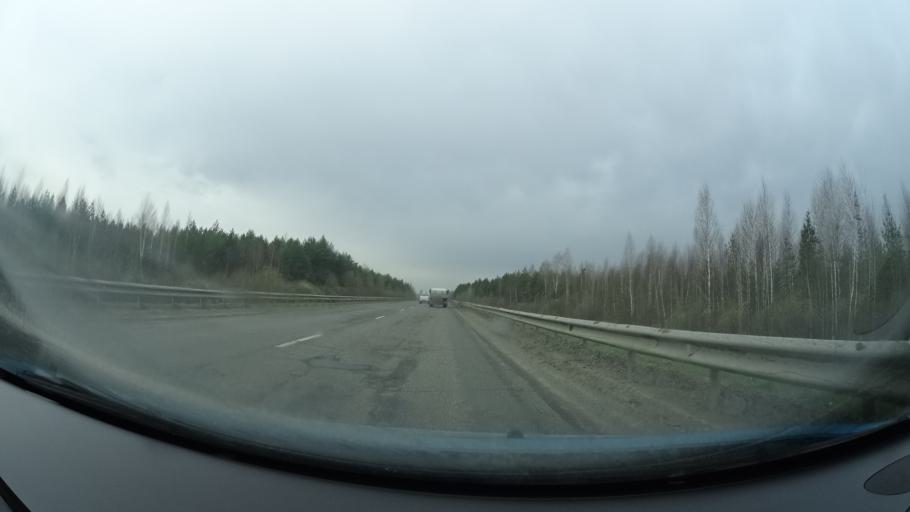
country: RU
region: Perm
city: Ust'-Kachka
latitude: 58.0832
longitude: 55.6670
